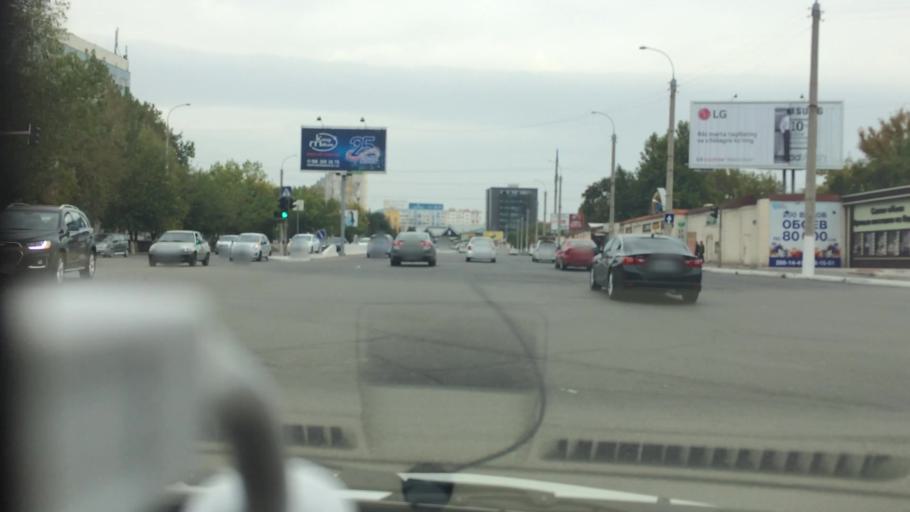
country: UZ
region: Toshkent
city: Salor
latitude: 41.3169
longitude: 69.3164
